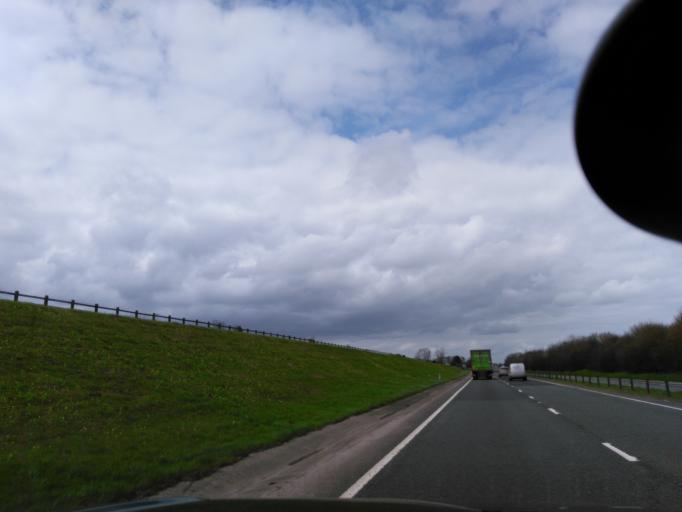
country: GB
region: England
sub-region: Gloucestershire
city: Coates
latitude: 51.7876
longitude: -2.0426
